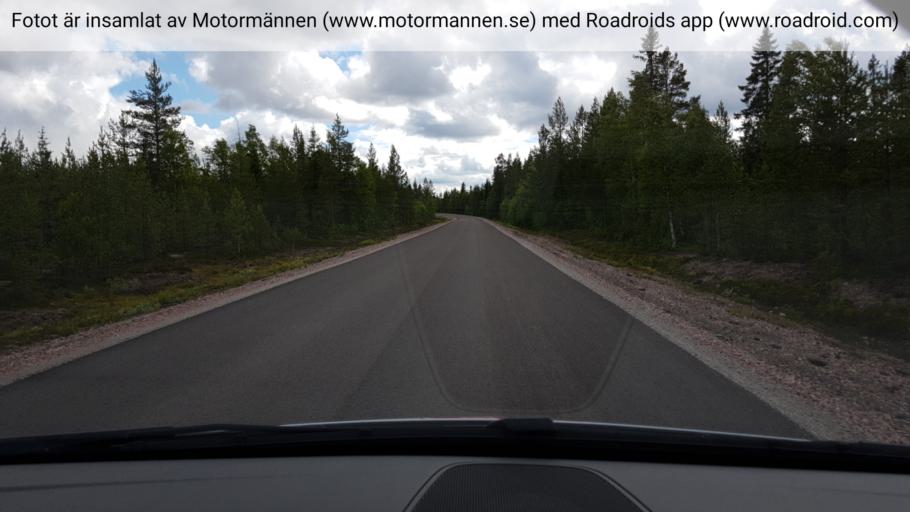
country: SE
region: Dalarna
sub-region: Alvdalens Kommun
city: AElvdalen
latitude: 61.6410
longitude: 14.1775
